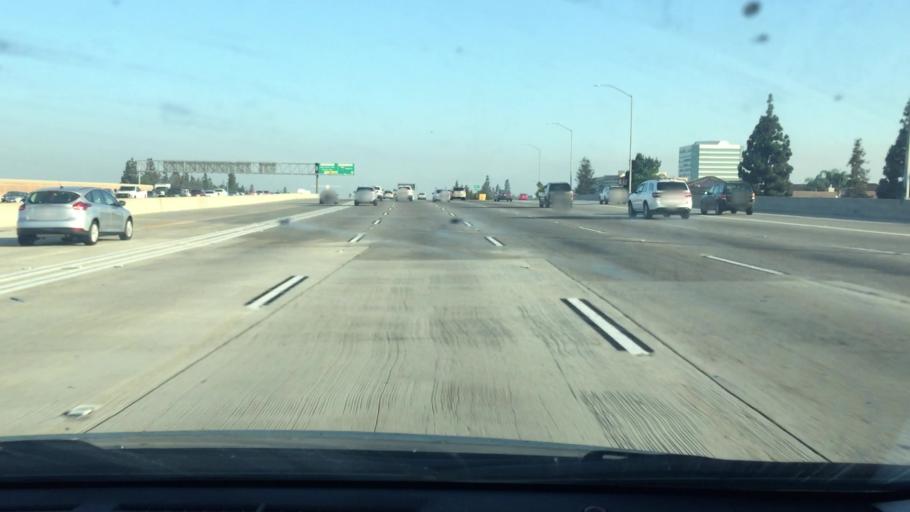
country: US
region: California
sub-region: Orange County
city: Orange
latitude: 33.7887
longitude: -117.8865
